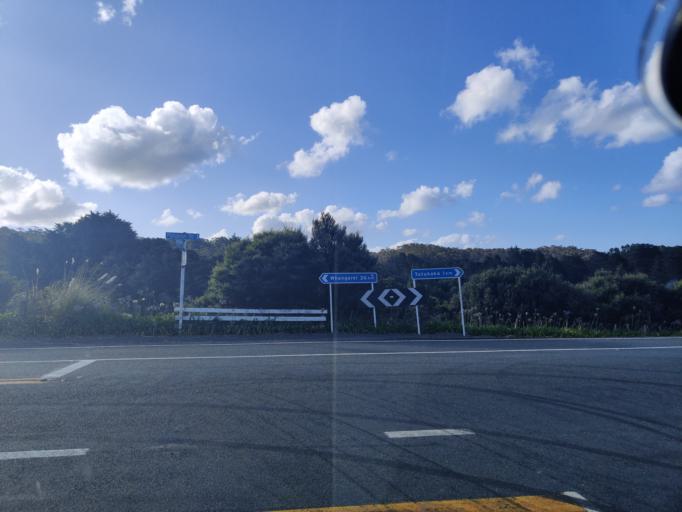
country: NZ
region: Northland
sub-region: Whangarei
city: Ngunguru
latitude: -35.6161
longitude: 174.5204
